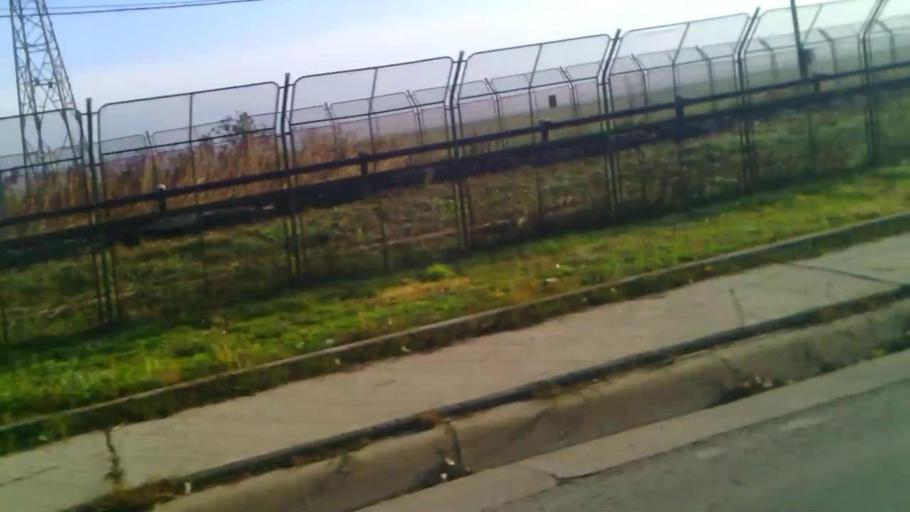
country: RO
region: Ilfov
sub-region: Comuna Popesti-Leordeni
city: Popesti-Leordeni
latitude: 44.3538
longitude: 26.1548
